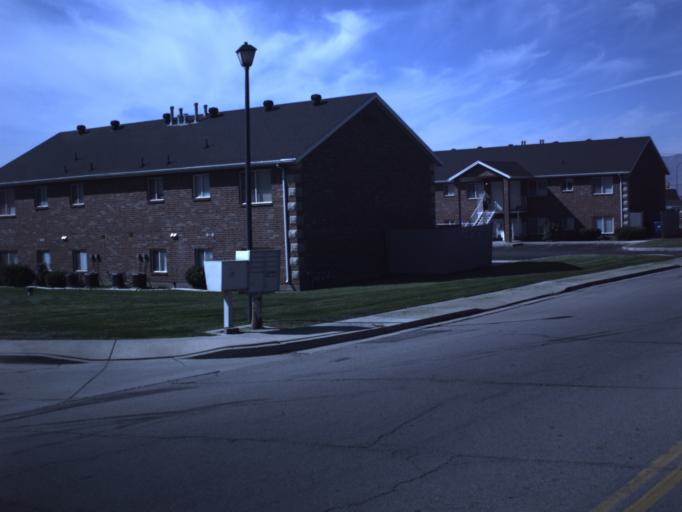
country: US
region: Utah
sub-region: Utah County
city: Lindon
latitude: 40.3522
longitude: -111.7297
